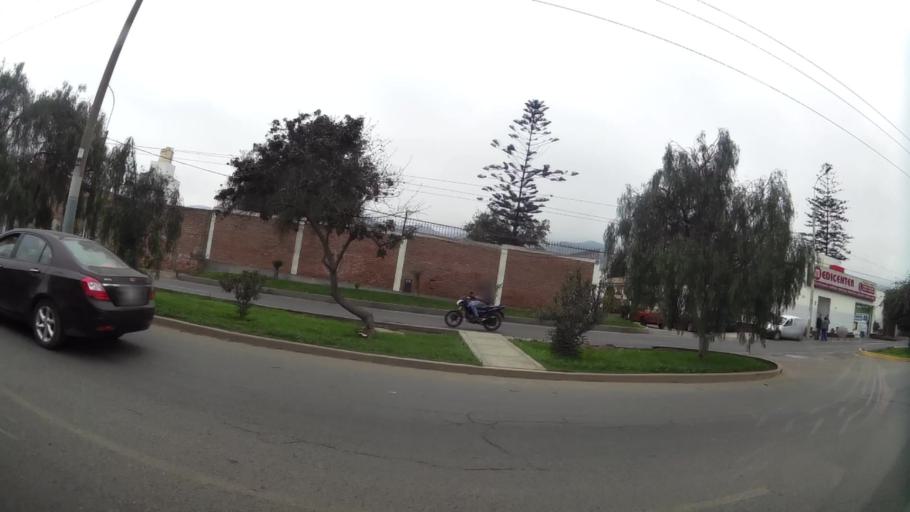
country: PE
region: Lima
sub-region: Lima
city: La Molina
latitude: -12.0861
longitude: -76.8964
